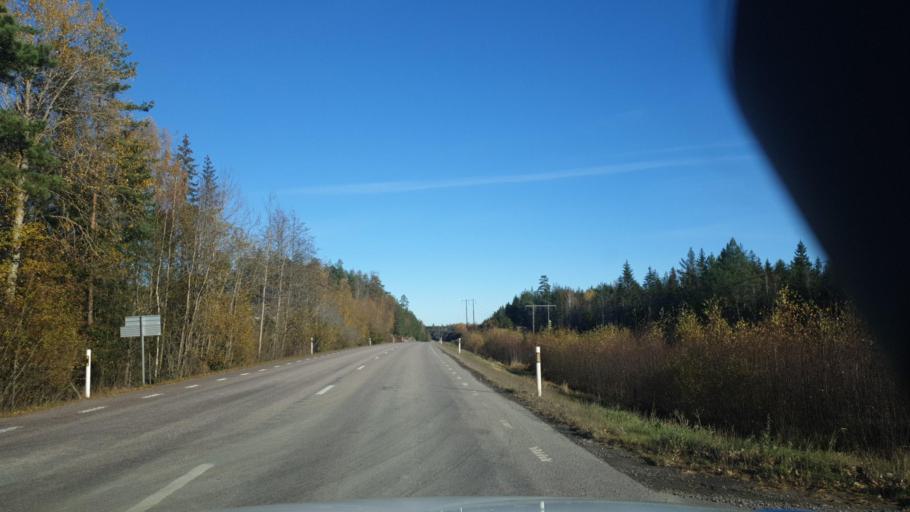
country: SE
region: Vaermland
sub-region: Karlstads Kommun
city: Edsvalla
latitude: 59.4180
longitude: 13.1877
